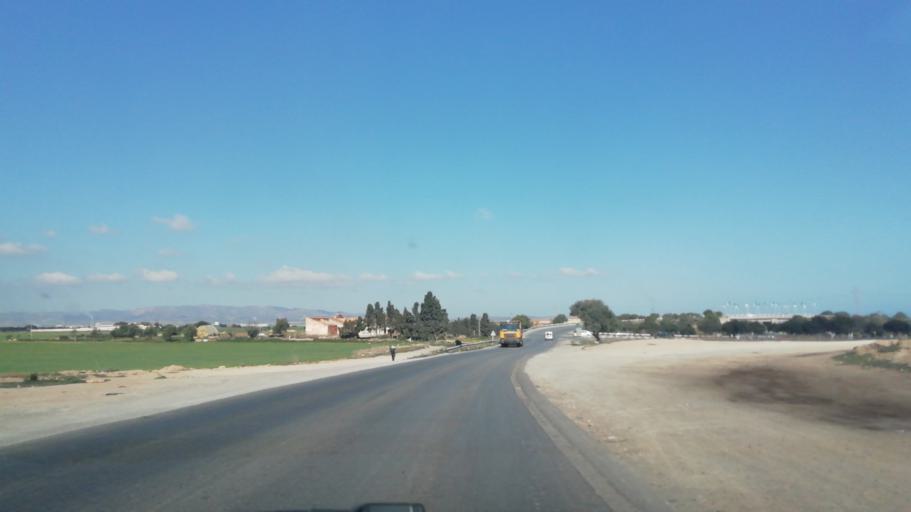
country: DZ
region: Oran
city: Ain el Bya
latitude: 35.7829
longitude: -0.2848
